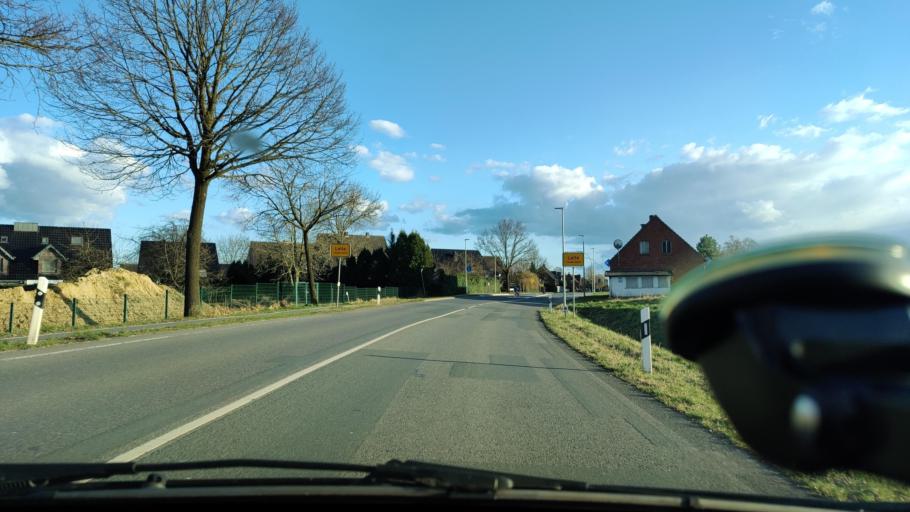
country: DE
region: North Rhine-Westphalia
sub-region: Regierungsbezirk Munster
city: Coesfeld
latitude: 51.9052
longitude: 7.1870
